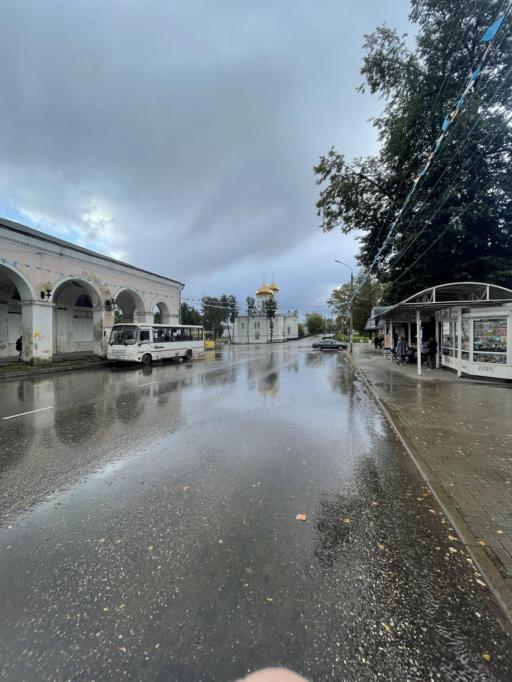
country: RU
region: Tverskaya
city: Vyshniy Volochek
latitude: 57.5837
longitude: 34.5588
